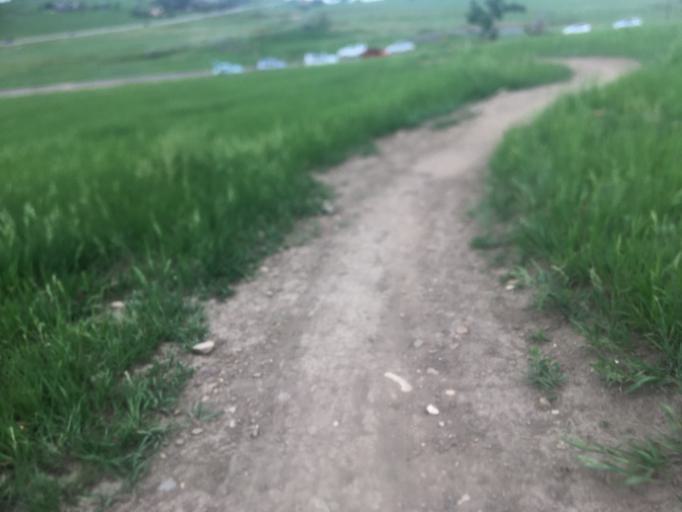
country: US
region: Colorado
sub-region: Boulder County
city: Superior
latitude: 39.9591
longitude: -105.2009
